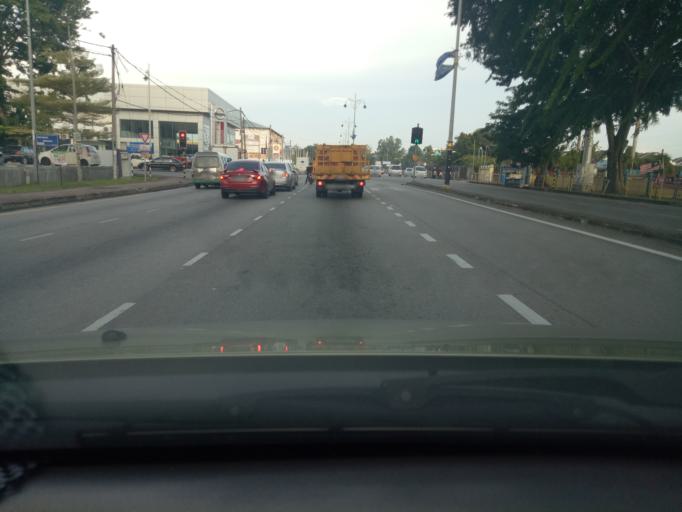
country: MY
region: Kedah
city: Alor Setar
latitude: 6.1275
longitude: 100.3521
